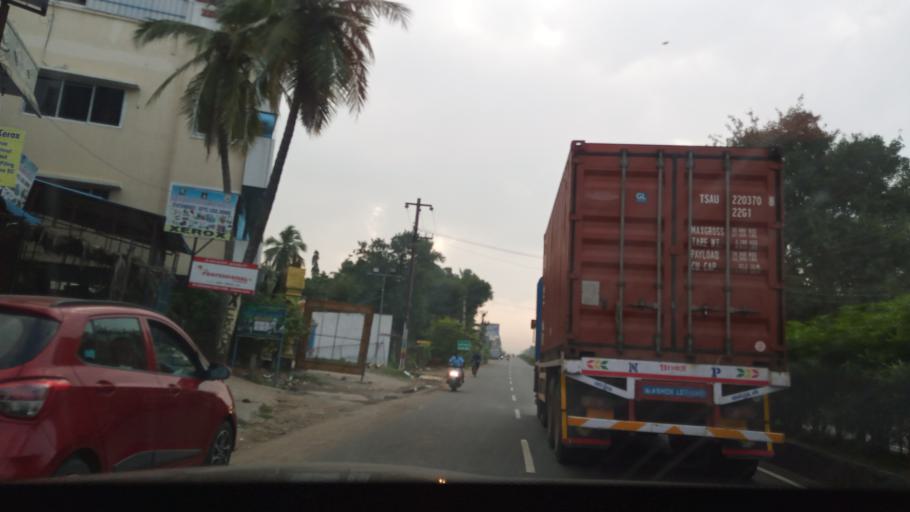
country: IN
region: Tamil Nadu
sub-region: Kancheepuram
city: Vengavasal
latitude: 12.8268
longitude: 80.1660
